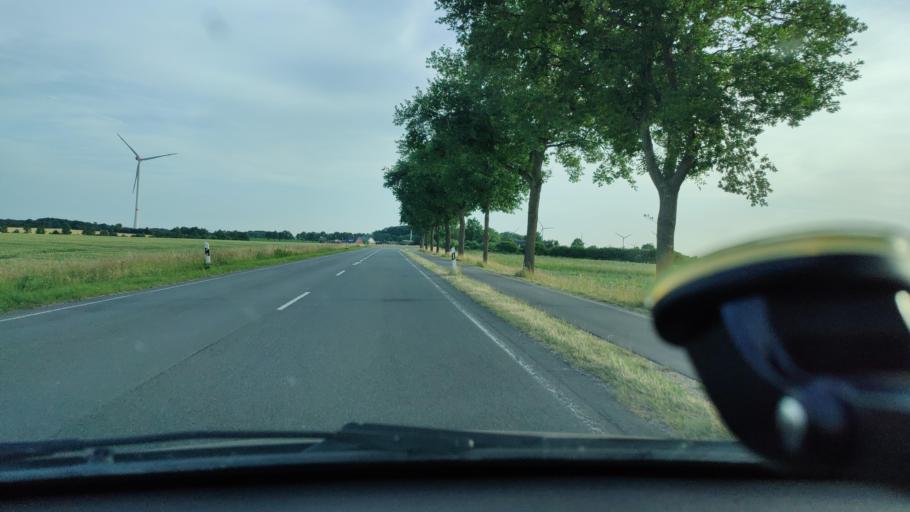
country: DE
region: North Rhine-Westphalia
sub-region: Regierungsbezirk Munster
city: Coesfeld
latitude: 52.0138
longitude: 7.1691
